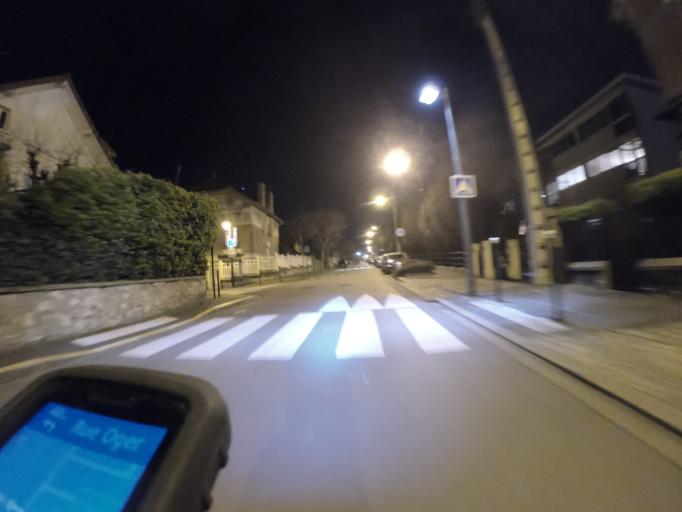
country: FR
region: Ile-de-France
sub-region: Departement des Hauts-de-Seine
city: Bourg-la-Reine
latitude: 48.7827
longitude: 2.3226
